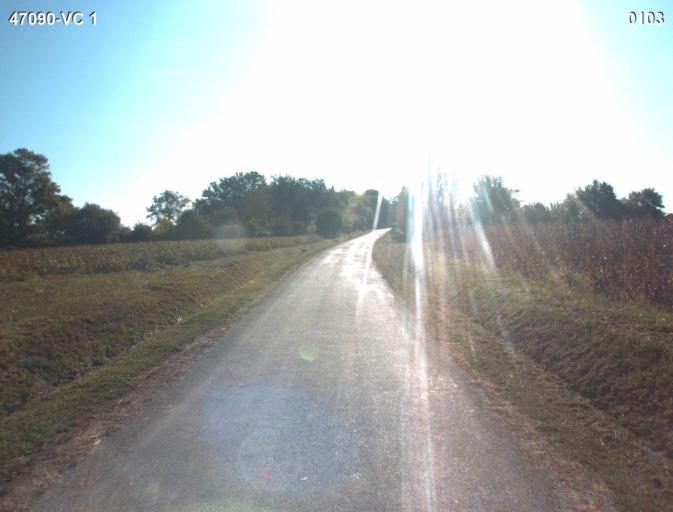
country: FR
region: Aquitaine
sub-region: Departement du Lot-et-Garonne
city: Nerac
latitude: 44.1702
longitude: 0.3739
